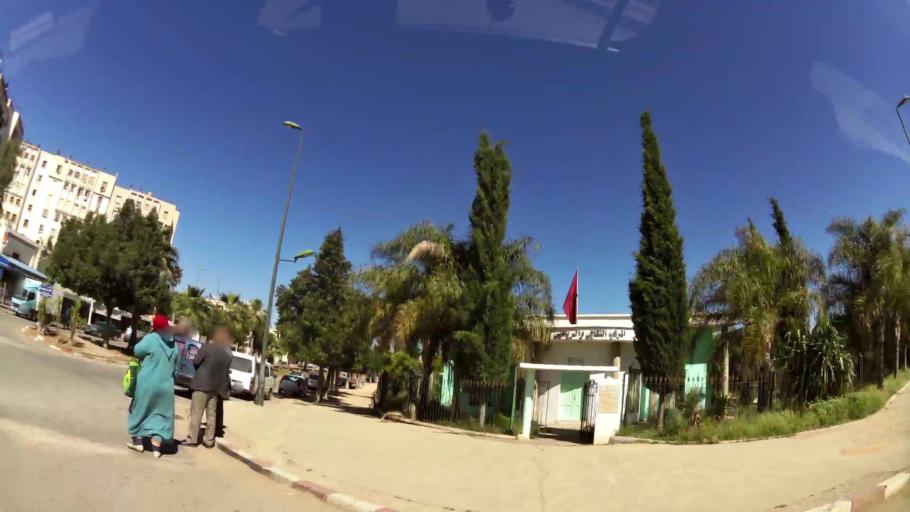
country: MA
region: Meknes-Tafilalet
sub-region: Meknes
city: Meknes
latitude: 33.9066
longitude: -5.5396
